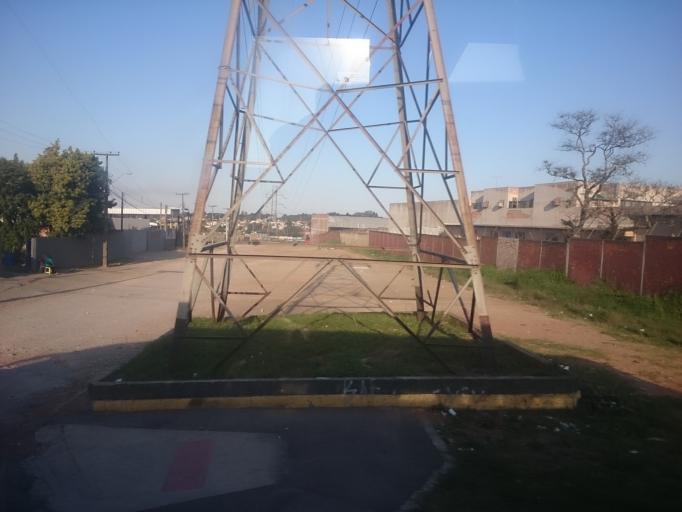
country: BR
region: Parana
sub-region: Sao Jose Dos Pinhais
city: Sao Jose dos Pinhais
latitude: -25.5251
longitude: -49.2964
